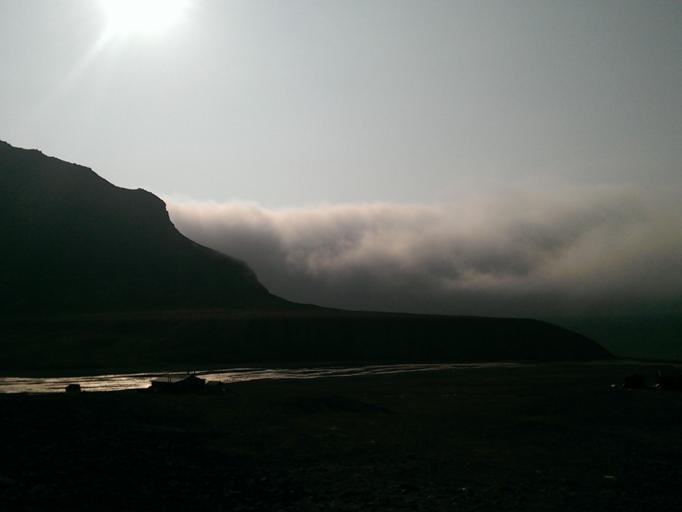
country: SJ
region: Svalbard
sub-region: Spitsbergen
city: Longyearbyen
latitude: 78.2255
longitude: 15.3284
